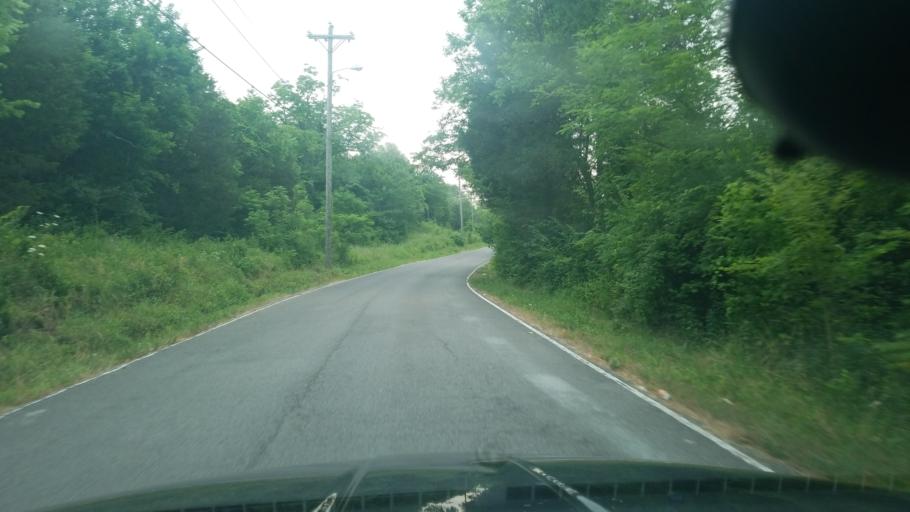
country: US
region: Tennessee
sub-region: Davidson County
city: Goodlettsville
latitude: 36.2494
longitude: -86.7557
